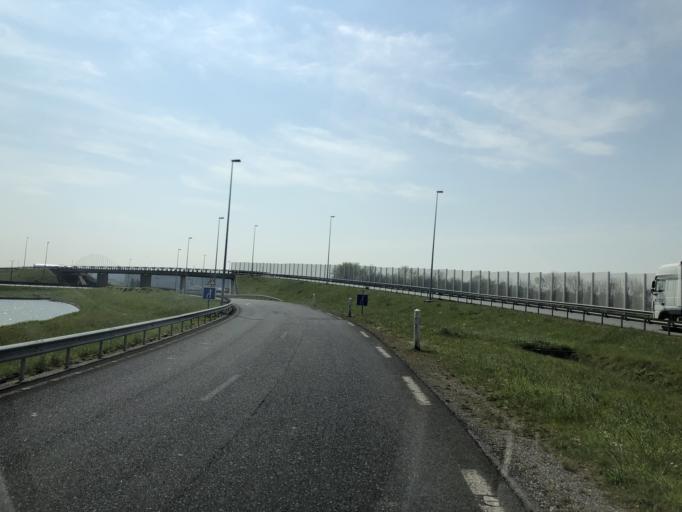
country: FR
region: Nord-Pas-de-Calais
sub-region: Departement du Pas-de-Calais
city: Coquelles
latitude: 50.9425
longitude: 1.8138
